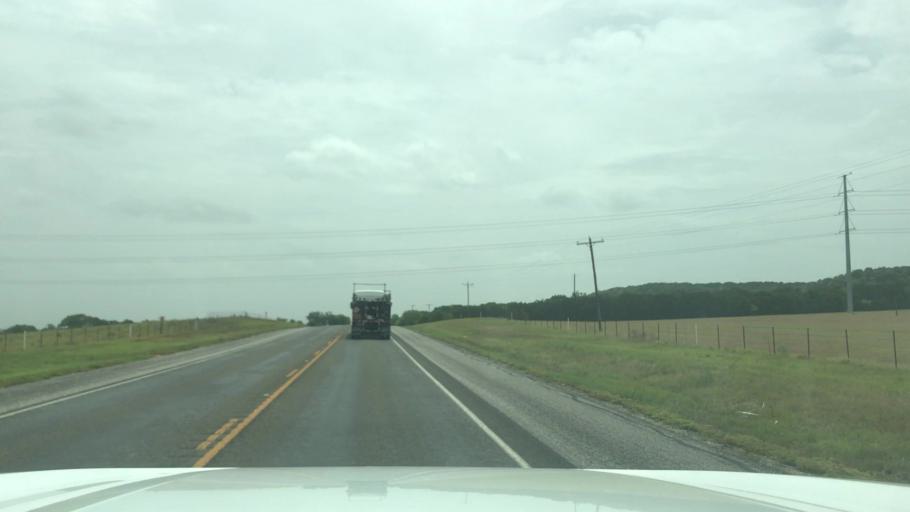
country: US
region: Texas
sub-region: Bosque County
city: Meridian
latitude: 31.8742
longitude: -97.6392
